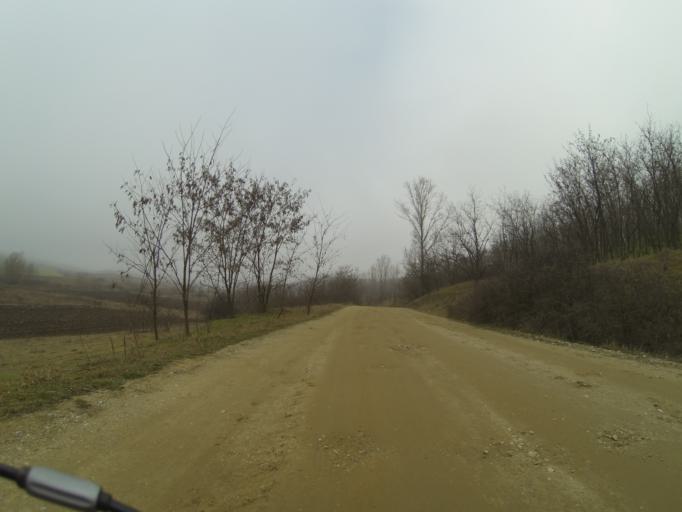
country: RO
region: Mehedinti
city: Padina Mica
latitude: 44.4838
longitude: 23.0330
